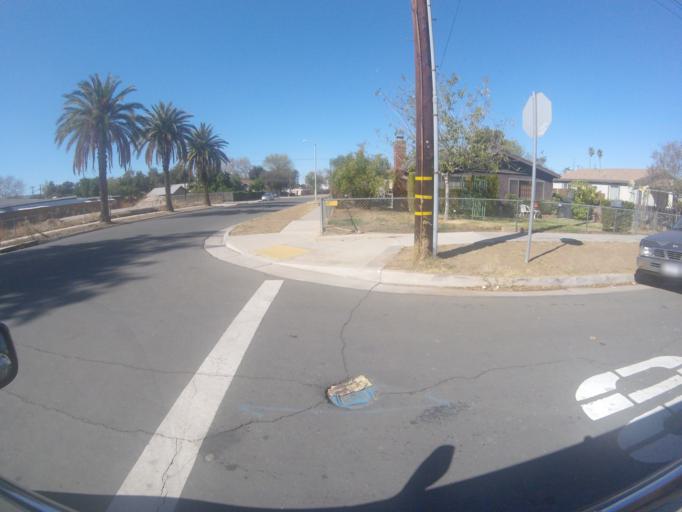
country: US
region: California
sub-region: San Bernardino County
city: Redlands
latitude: 34.0654
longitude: -117.1901
